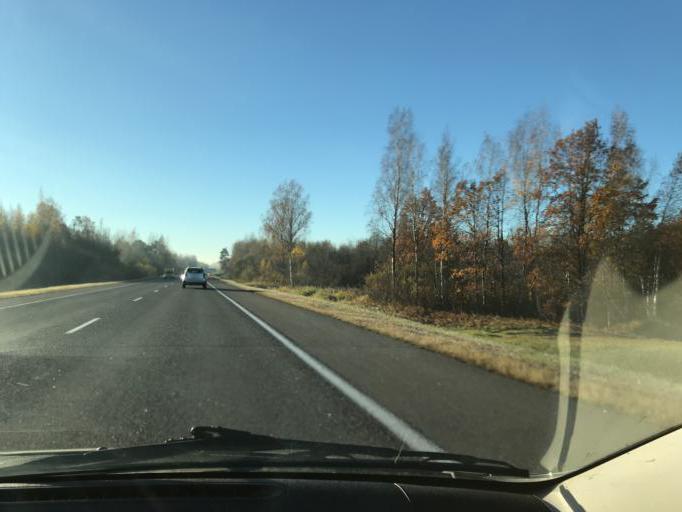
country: BY
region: Vitebsk
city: Vitebsk
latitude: 54.9686
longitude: 30.3524
